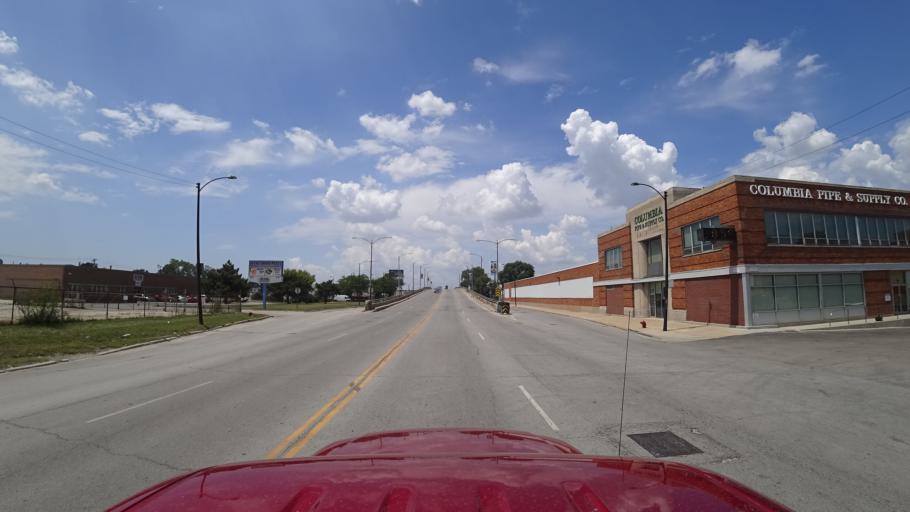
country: US
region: Illinois
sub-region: Cook County
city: Chicago
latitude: 41.8234
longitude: -87.6538
